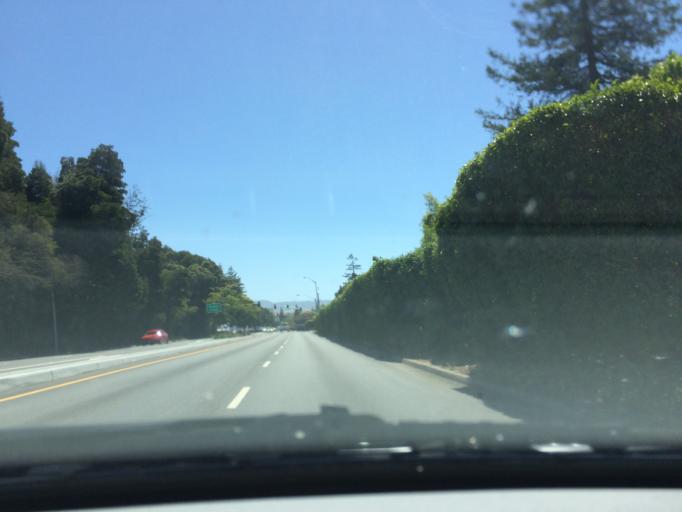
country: US
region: California
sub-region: Santa Clara County
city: Palo Alto
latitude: 37.4321
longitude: -122.1368
